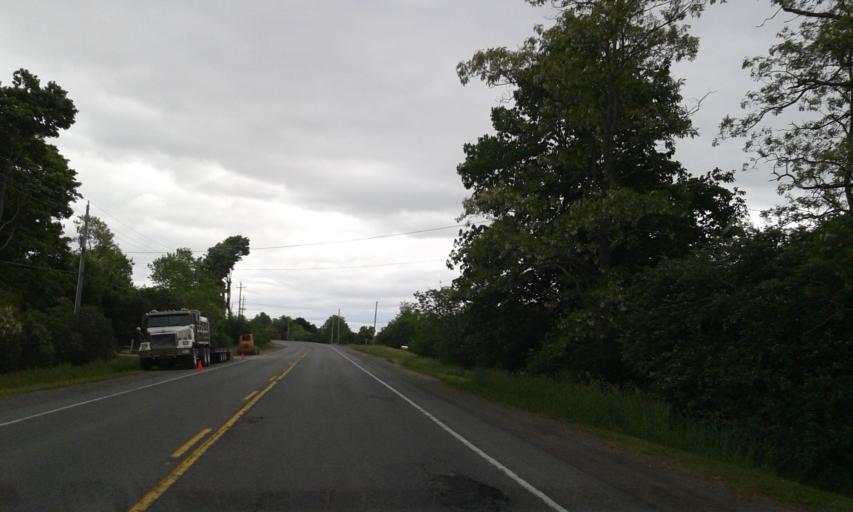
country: CA
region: Ontario
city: Belleville
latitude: 43.9646
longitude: -77.4841
